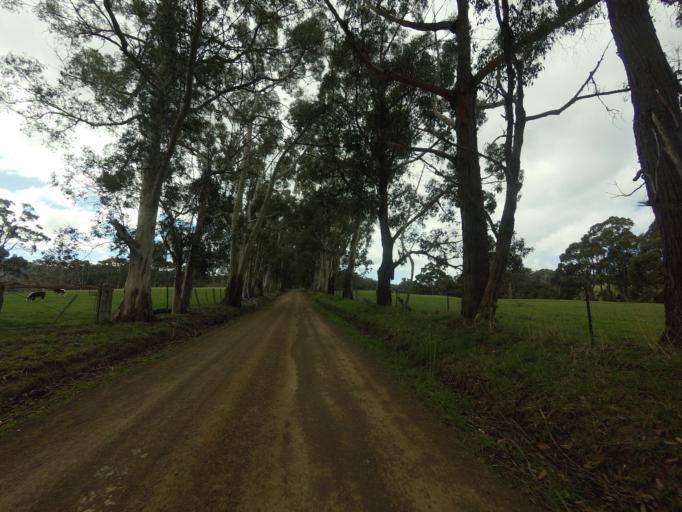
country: AU
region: Tasmania
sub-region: Huon Valley
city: Geeveston
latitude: -43.4289
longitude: 146.9929
